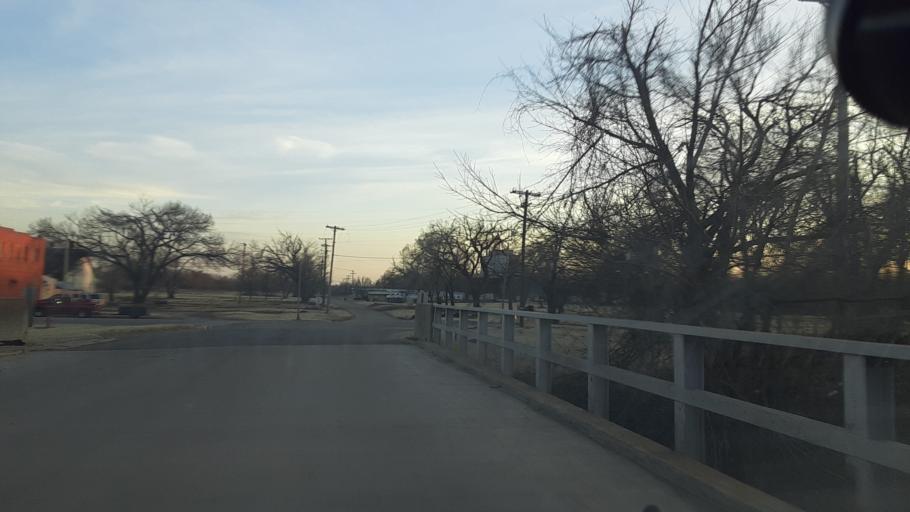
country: US
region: Oklahoma
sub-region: Logan County
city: Guthrie
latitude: 35.8786
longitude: -97.4316
